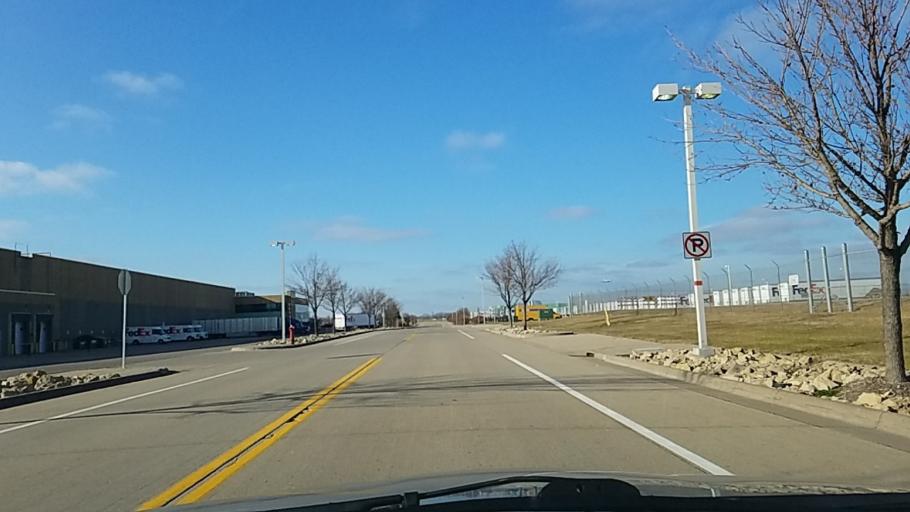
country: US
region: Minnesota
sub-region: Hennepin County
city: Richfield
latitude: 44.8830
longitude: -93.2310
